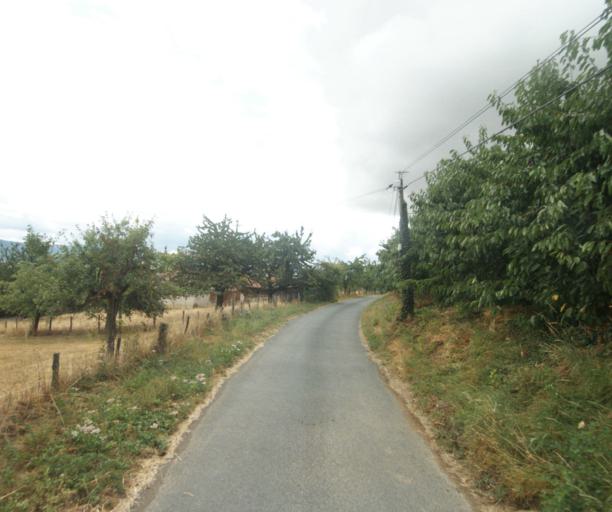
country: FR
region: Rhone-Alpes
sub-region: Departement du Rhone
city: Bessenay
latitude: 45.7793
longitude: 4.5302
